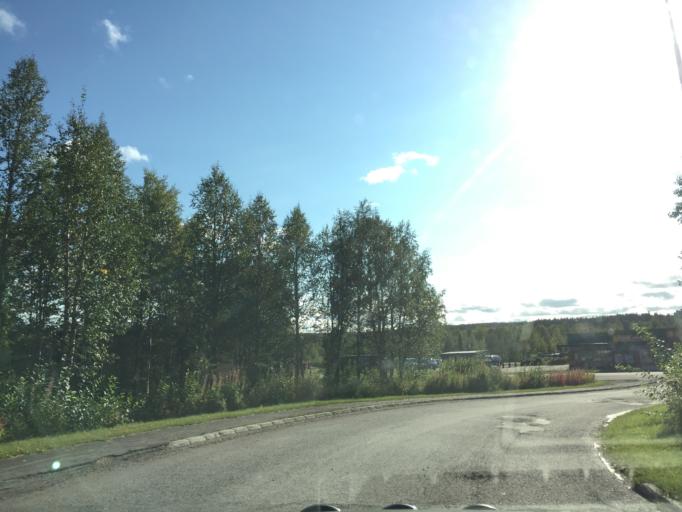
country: SE
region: Norrbotten
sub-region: Gallivare Kommun
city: Malmberget
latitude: 67.6489
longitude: 21.0476
